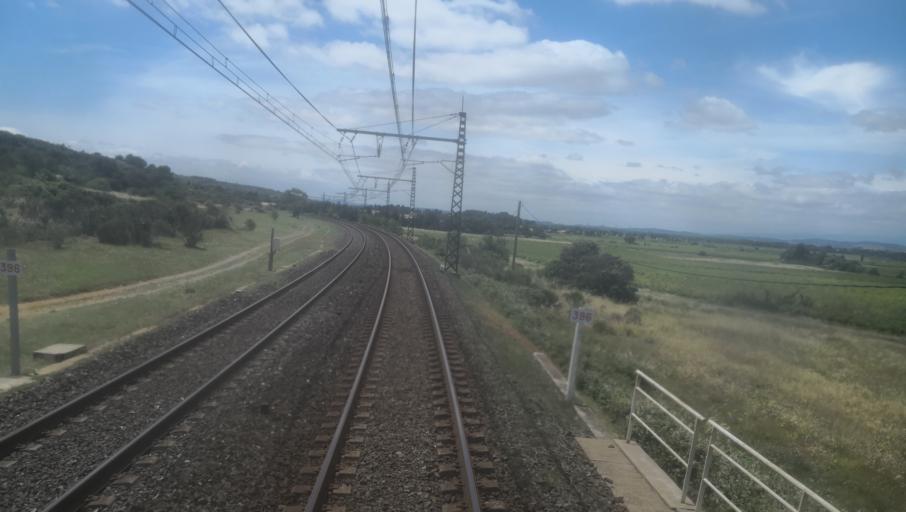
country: FR
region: Languedoc-Roussillon
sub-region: Departement de l'Aude
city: Marcorignan
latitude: 43.2155
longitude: 2.9181
